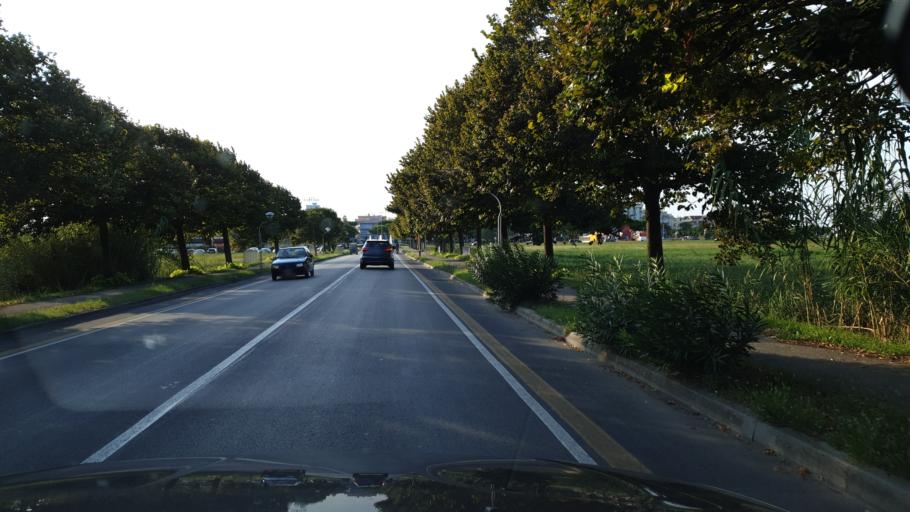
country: IT
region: Emilia-Romagna
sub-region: Provincia di Rimini
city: Misano Adriatico
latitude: 43.9812
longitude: 12.6927
